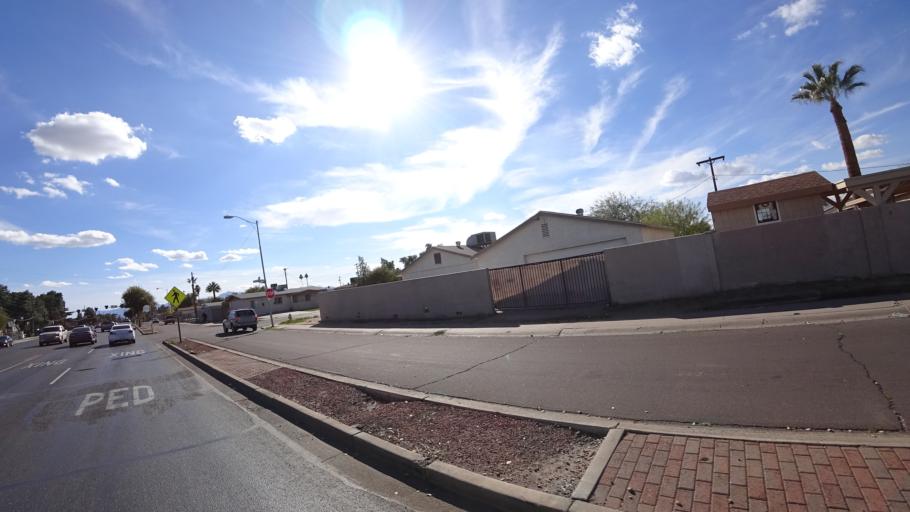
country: US
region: Arizona
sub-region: Maricopa County
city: Tolleson
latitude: 33.4925
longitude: -112.2206
